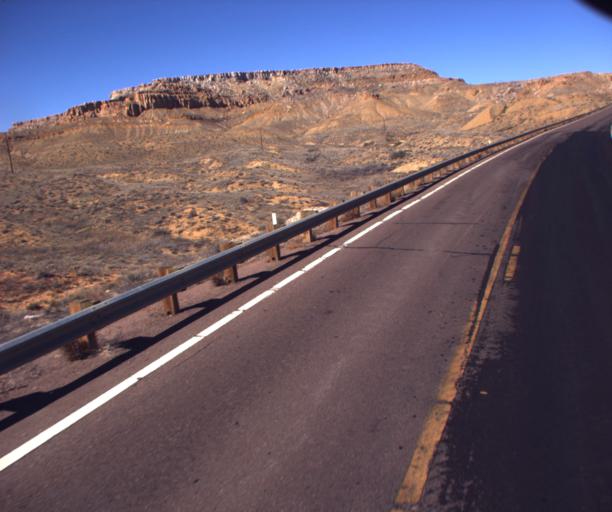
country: US
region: Arizona
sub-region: Navajo County
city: First Mesa
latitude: 35.7968
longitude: -110.5127
